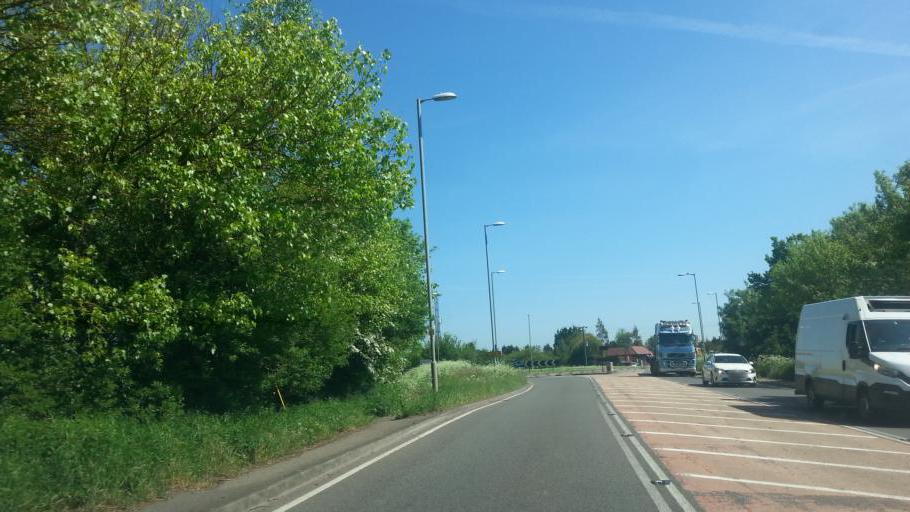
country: GB
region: England
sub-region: Cambridgeshire
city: Warboys
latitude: 52.3881
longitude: -0.0922
